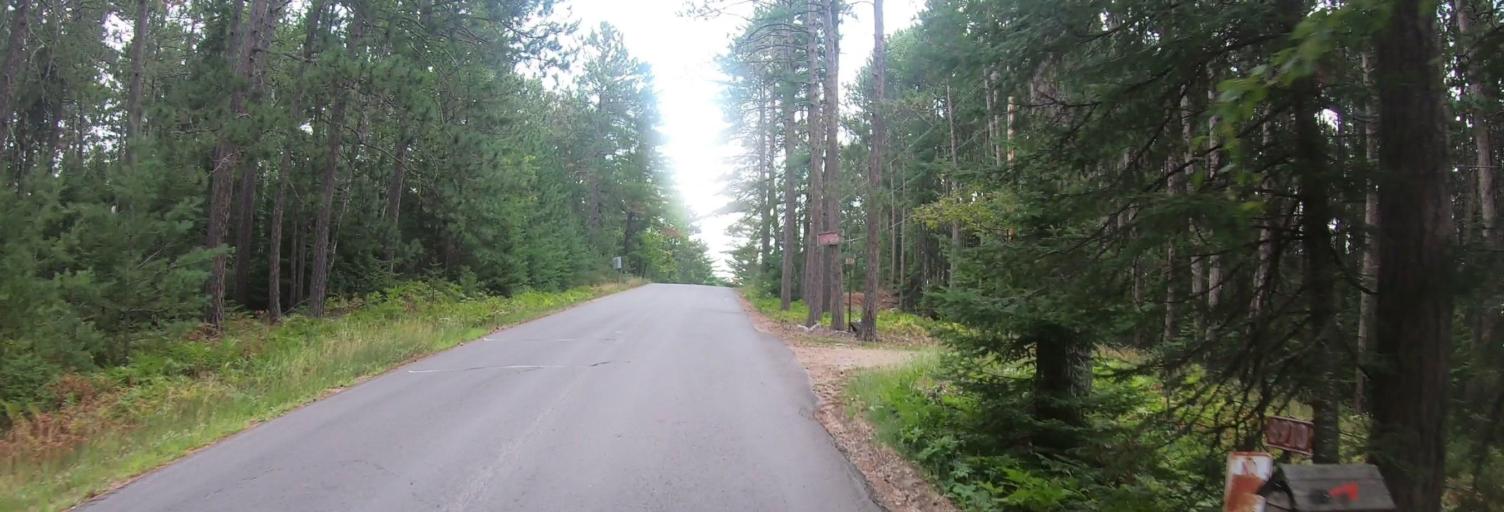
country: US
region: Minnesota
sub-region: Saint Louis County
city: Mountain Iron
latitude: 47.9543
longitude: -92.6367
